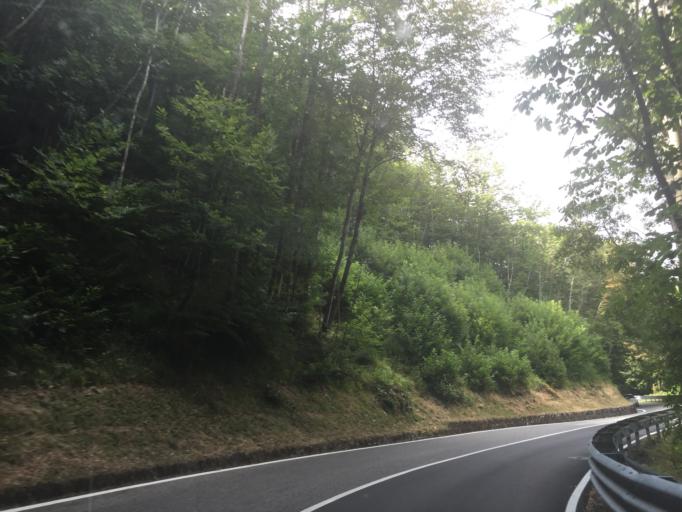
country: IT
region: Tuscany
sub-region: Provincia di Pistoia
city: Cutigliano
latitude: 44.1161
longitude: 10.7315
